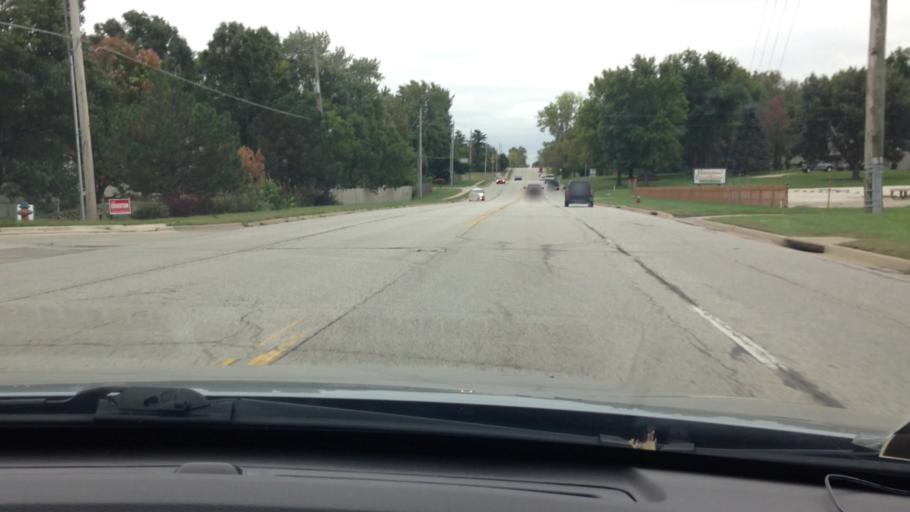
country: US
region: Kansas
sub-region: Leavenworth County
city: Leavenworth
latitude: 39.2742
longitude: -94.9280
